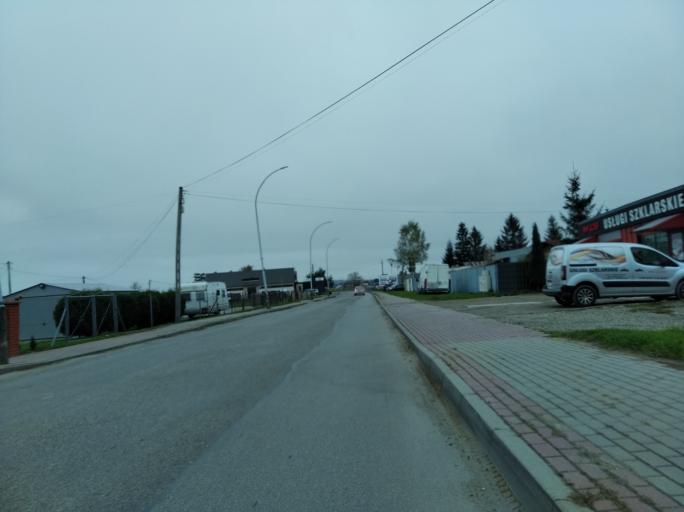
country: PL
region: Subcarpathian Voivodeship
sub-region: Krosno
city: Krosno
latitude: 49.6917
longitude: 21.7406
